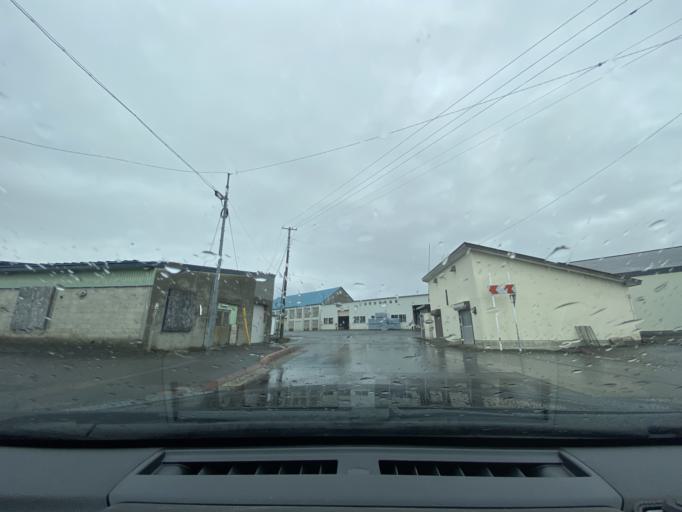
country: JP
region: Hokkaido
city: Fukagawa
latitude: 43.8101
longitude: 141.9323
